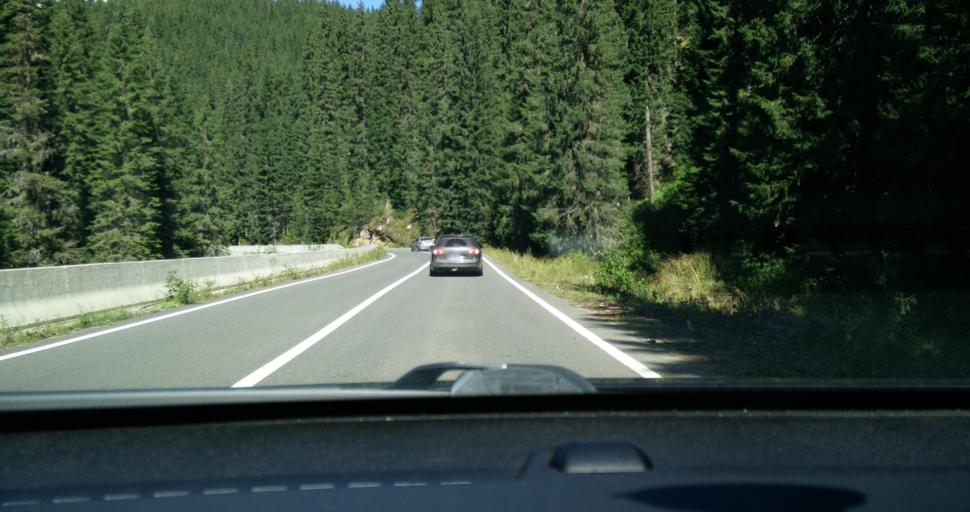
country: RO
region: Hunedoara
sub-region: Oras Petrila
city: Petrila
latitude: 45.5229
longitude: 23.6475
